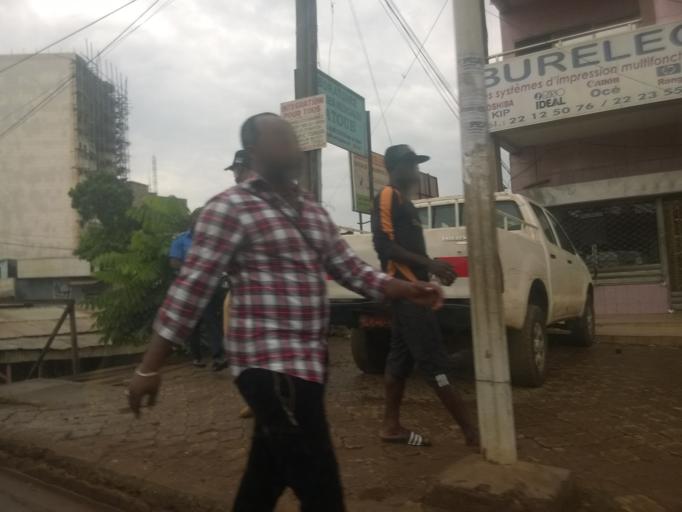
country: CM
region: Centre
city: Yaounde
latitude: 3.8704
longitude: 11.5242
